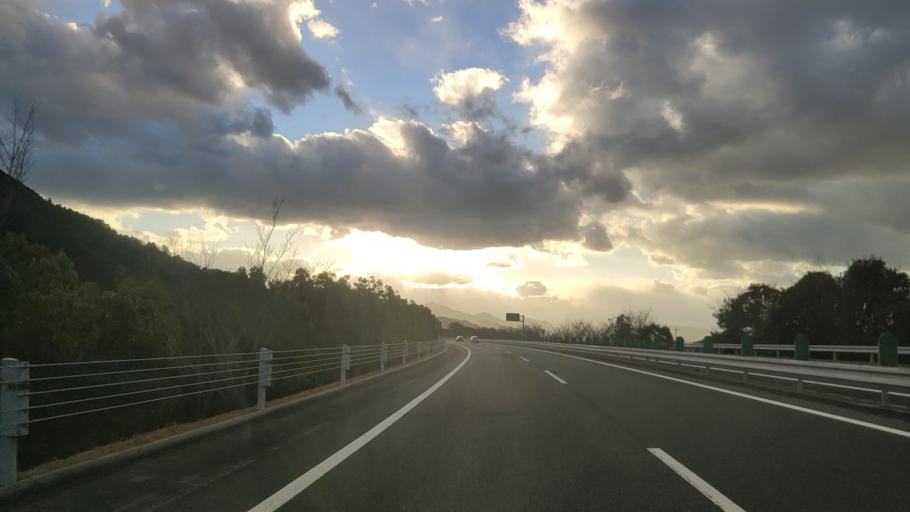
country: JP
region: Ehime
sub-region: Shikoku-chuo Shi
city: Matsuyama
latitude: 33.7933
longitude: 132.8999
